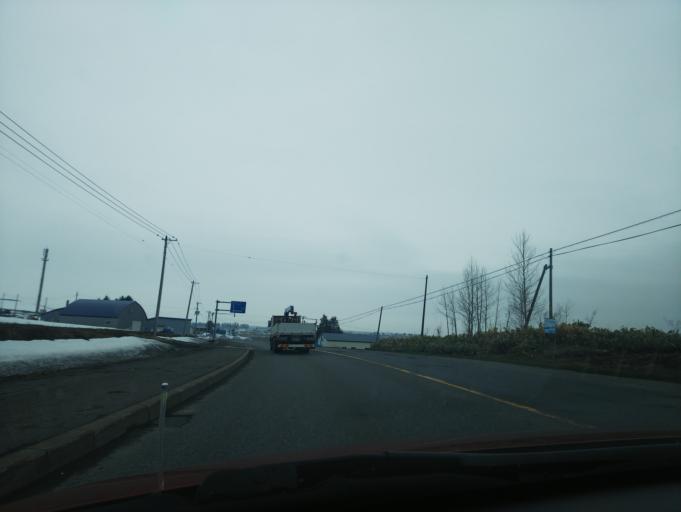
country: JP
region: Hokkaido
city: Nayoro
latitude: 44.0626
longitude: 142.4019
